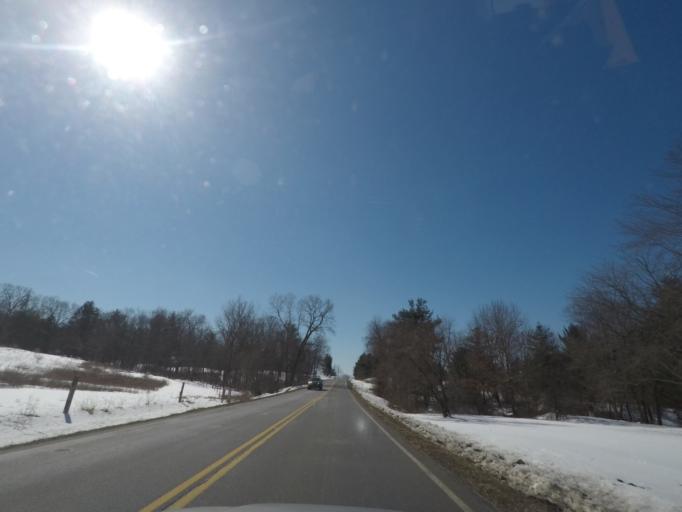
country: US
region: New York
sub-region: Saratoga County
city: Stillwater
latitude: 42.9960
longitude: -73.5969
